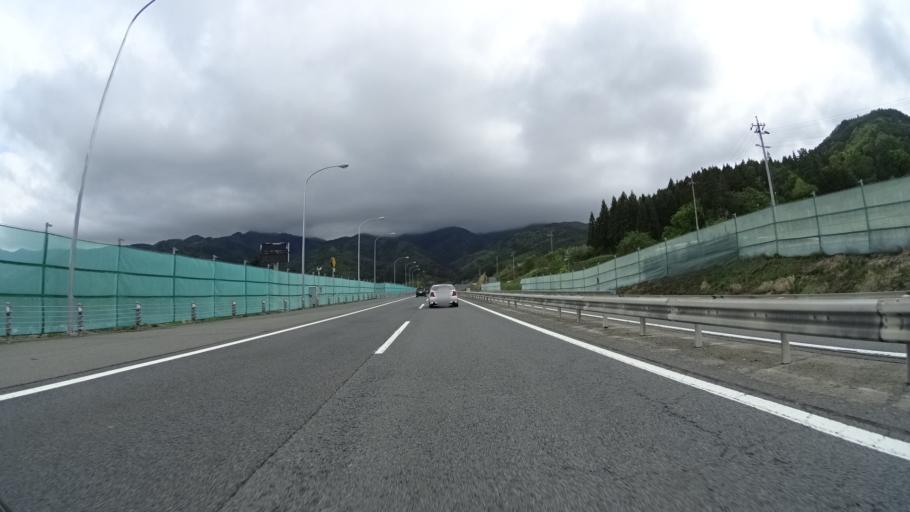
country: JP
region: Nagano
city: Nagano-shi
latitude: 36.5248
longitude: 138.0781
